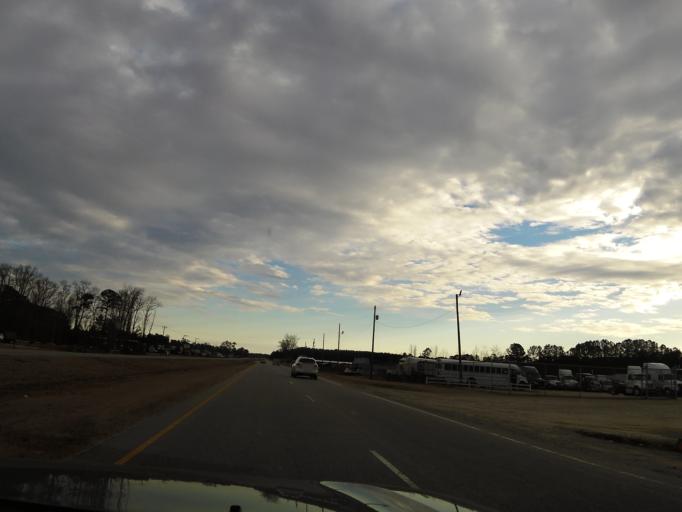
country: US
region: North Carolina
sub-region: Nash County
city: Sharpsburg
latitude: 35.9019
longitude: -77.8267
